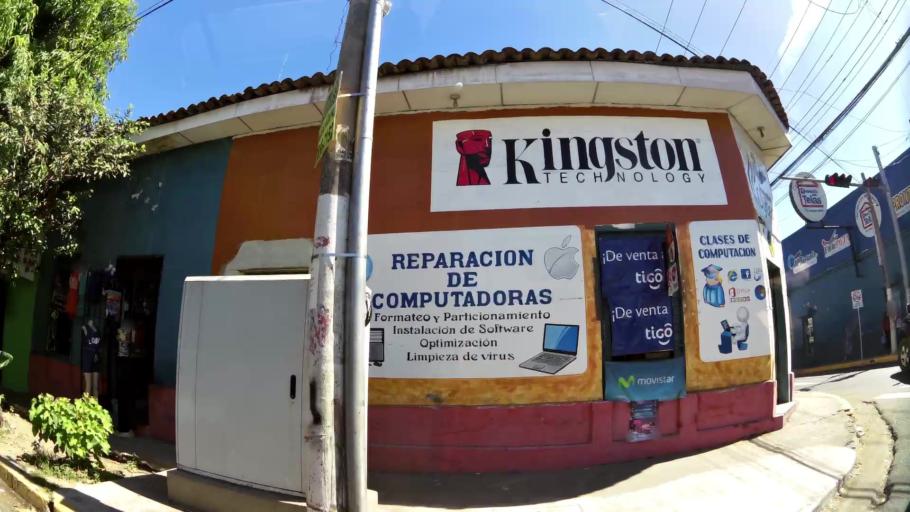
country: SV
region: La Libertad
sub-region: Distrito de Quezaltepeque
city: Quezaltepeque
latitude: 13.8315
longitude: -89.2717
